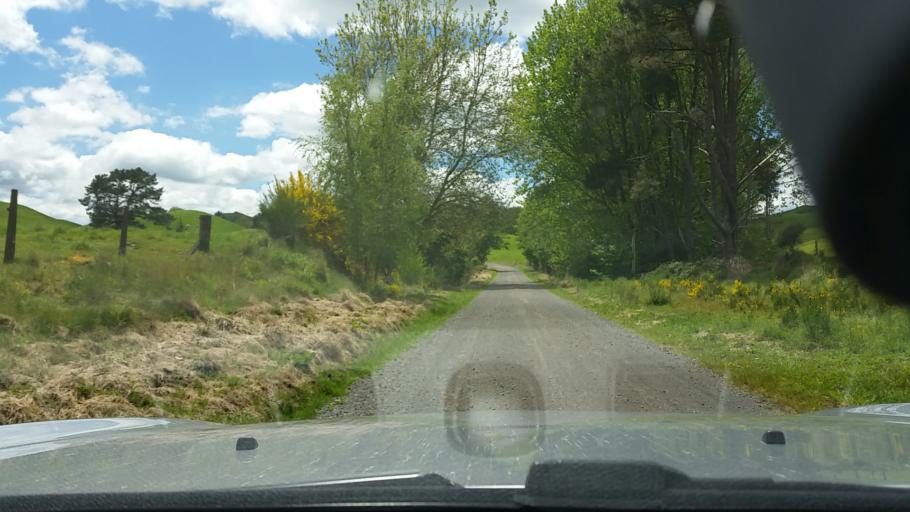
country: NZ
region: Waikato
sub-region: South Waikato District
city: Tokoroa
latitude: -38.3848
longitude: 176.0791
